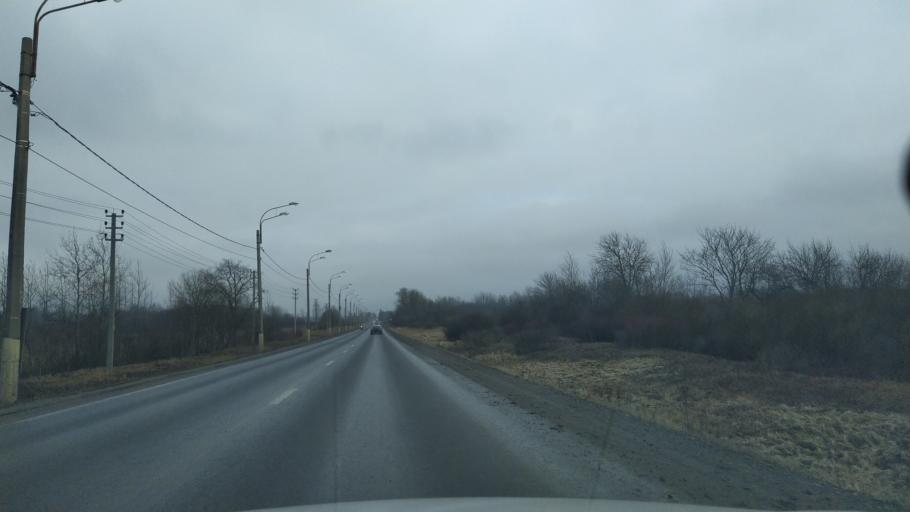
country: RU
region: St.-Petersburg
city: Aleksandrovskaya
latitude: 59.7139
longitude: 30.3027
